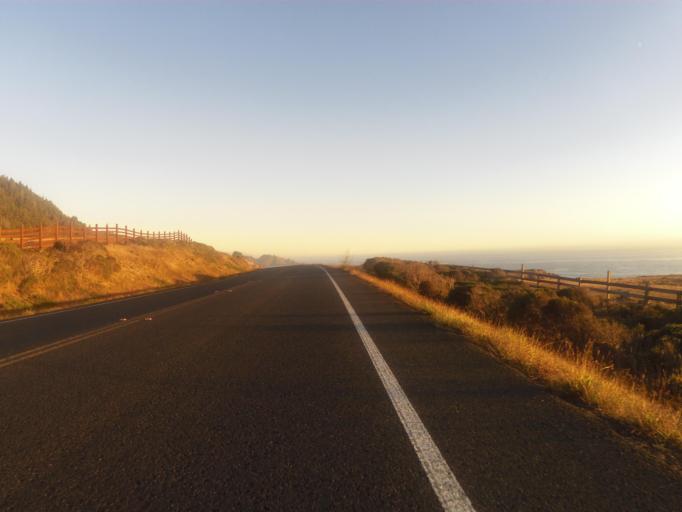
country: US
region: California
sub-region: Sonoma County
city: Sea Ranch
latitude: 38.6306
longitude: -123.3858
